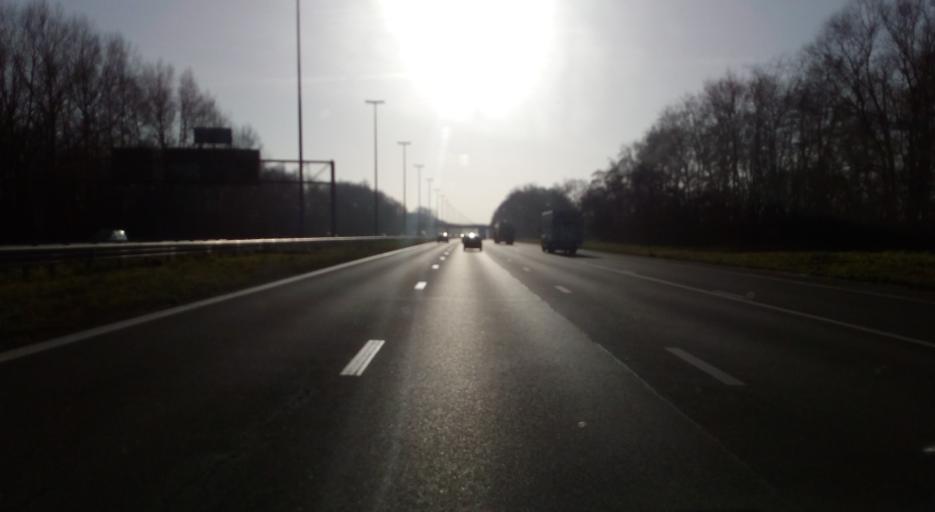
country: BE
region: Wallonia
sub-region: Province du Brabant Wallon
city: Braine-le-Chateau
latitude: 50.6582
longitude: 4.3102
